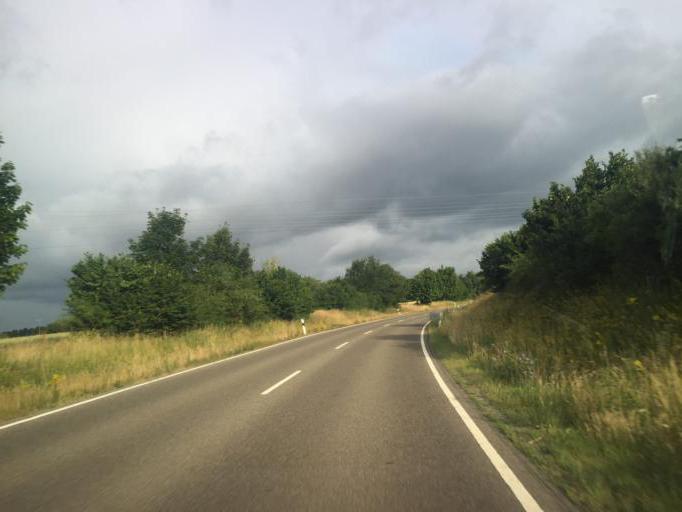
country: DE
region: Baden-Wuerttemberg
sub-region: Regierungsbezirk Stuttgart
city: Nufringen
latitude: 48.6355
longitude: 8.8848
